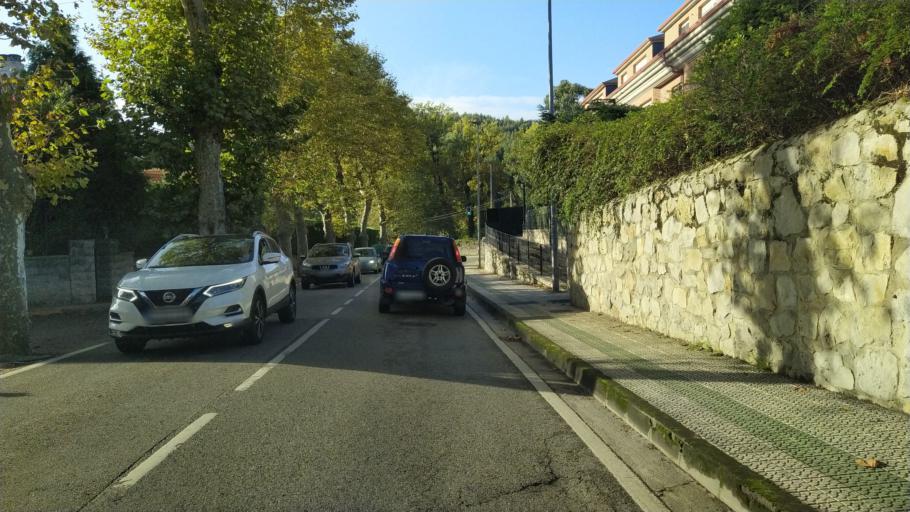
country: ES
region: Cantabria
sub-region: Provincia de Cantabria
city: Santa Cruz de Bezana
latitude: 43.4432
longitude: -3.9298
